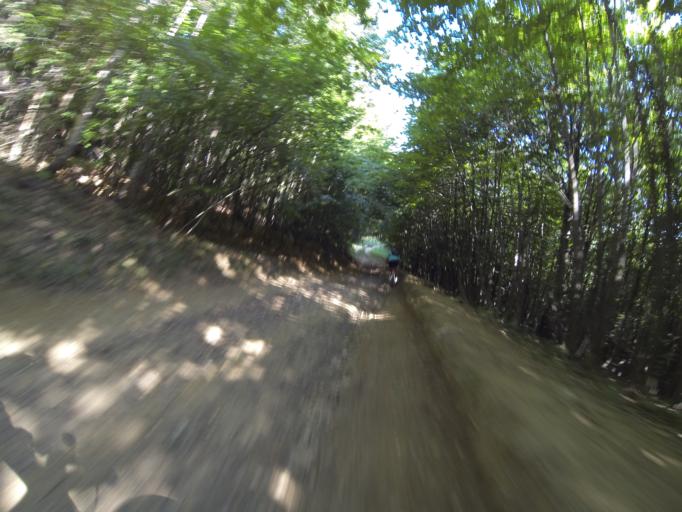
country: RO
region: Valcea
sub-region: Comuna Vaideeni
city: Vaideeni
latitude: 45.2274
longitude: 23.9660
